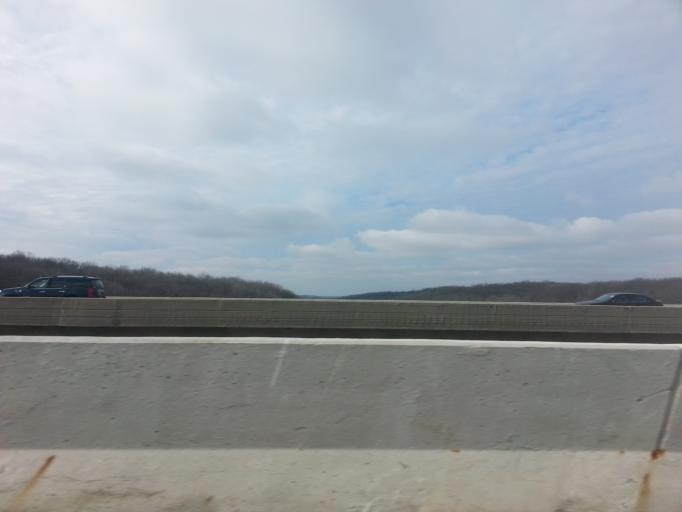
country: US
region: Illinois
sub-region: Winnebago County
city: Cherry Valley
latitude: 42.1832
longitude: -89.0237
